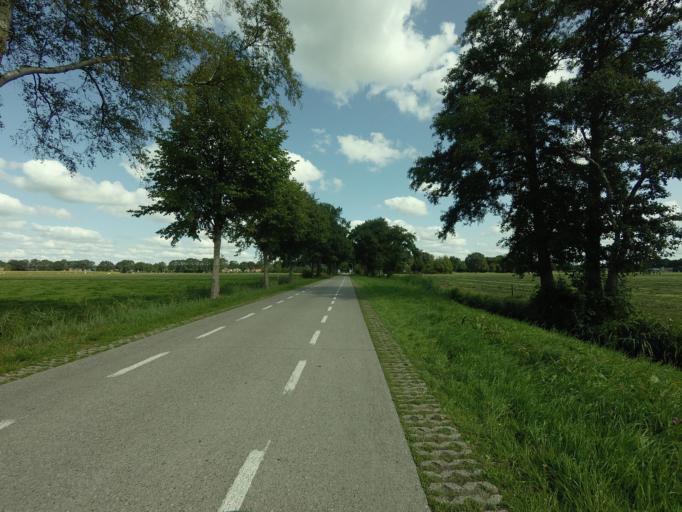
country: NL
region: Overijssel
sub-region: Gemeente Staphorst
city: Staphorst
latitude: 52.6105
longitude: 6.2596
